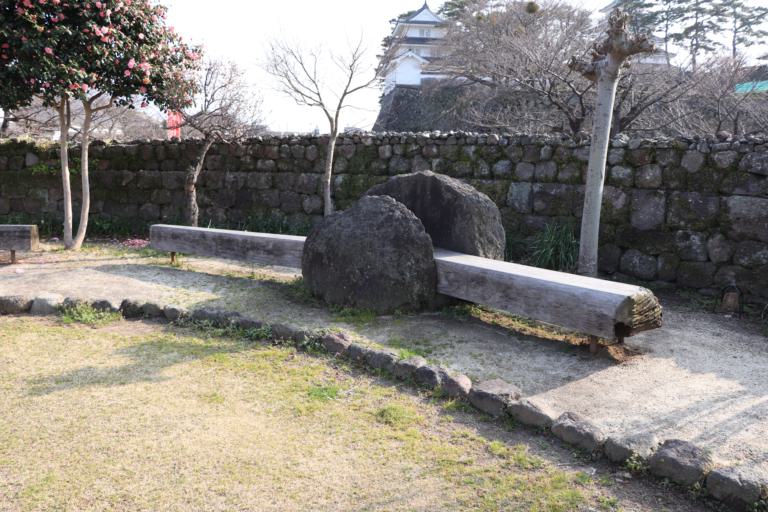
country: JP
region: Nagasaki
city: Shimabara
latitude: 32.7910
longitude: 130.3676
